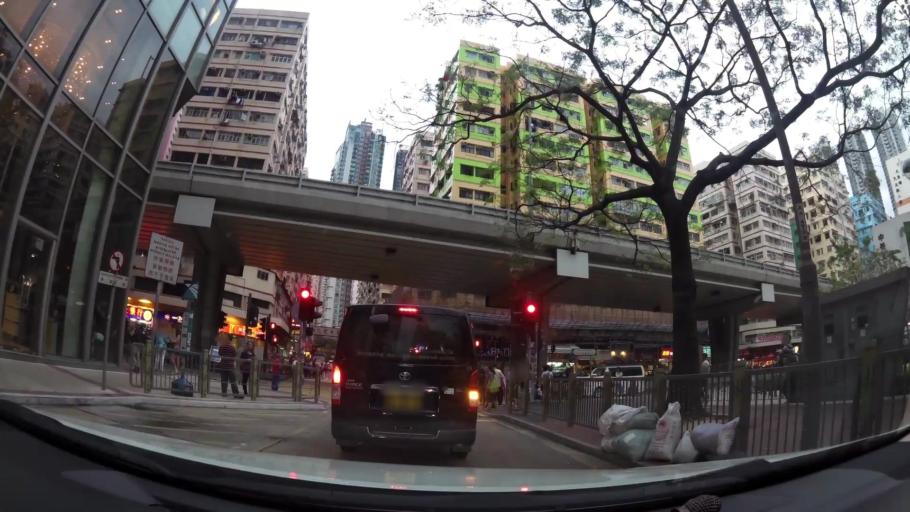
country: HK
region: Sham Shui Po
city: Sham Shui Po
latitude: 22.3214
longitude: 114.1621
